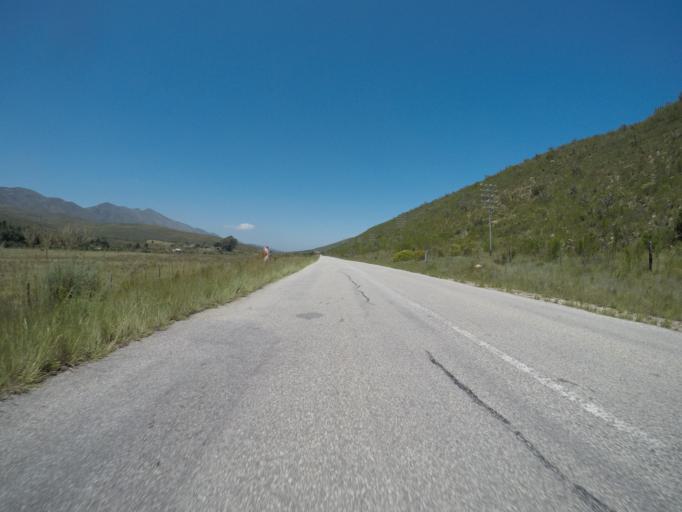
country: ZA
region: Eastern Cape
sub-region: Cacadu District Municipality
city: Kareedouw
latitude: -33.9015
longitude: 24.1290
